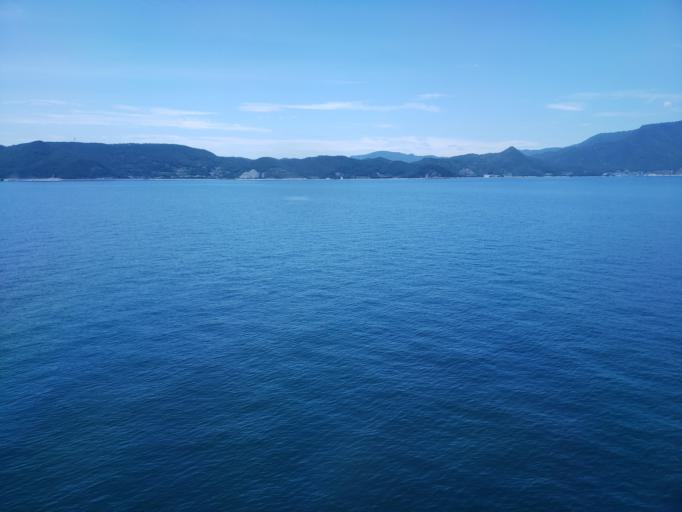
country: JP
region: Kagawa
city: Tonosho
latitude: 34.4260
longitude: 134.2756
